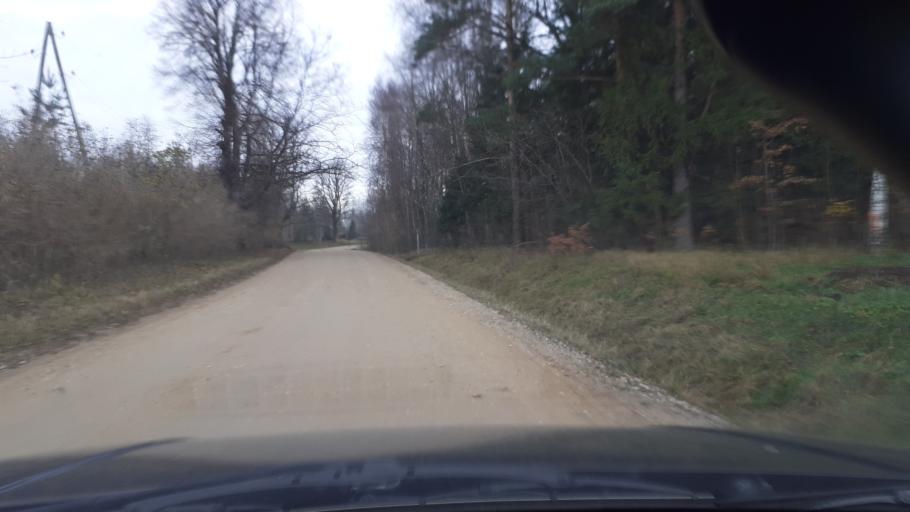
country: LV
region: Alsunga
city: Alsunga
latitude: 56.9479
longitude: 21.6413
